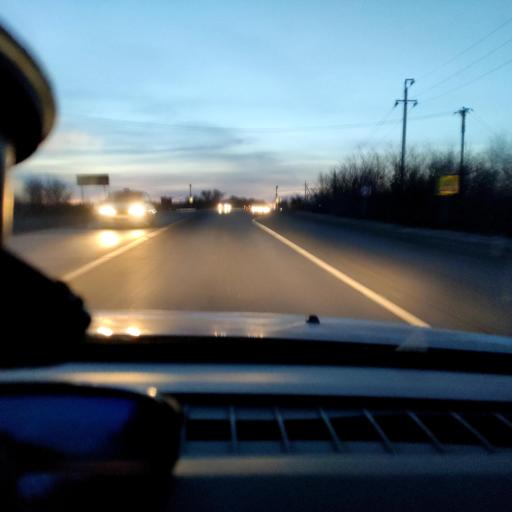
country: RU
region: Samara
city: Novokuybyshevsk
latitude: 53.0850
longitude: 50.0651
